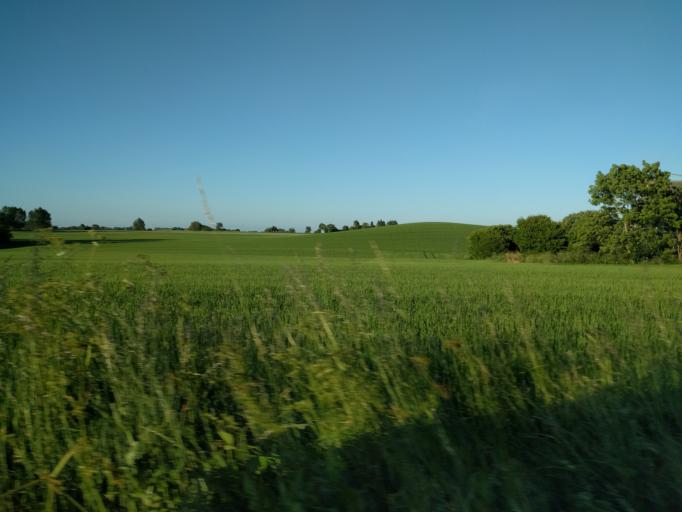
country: DK
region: South Denmark
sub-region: Kerteminde Kommune
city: Kerteminde
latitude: 55.5556
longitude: 10.6536
